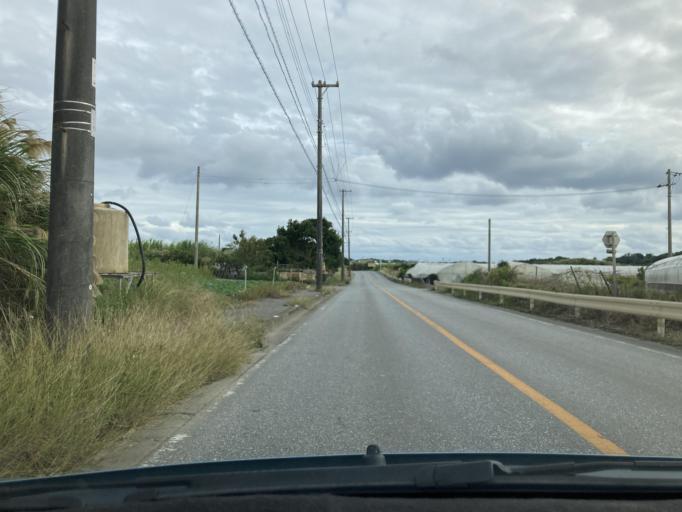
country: JP
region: Okinawa
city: Itoman
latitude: 26.1155
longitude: 127.6974
